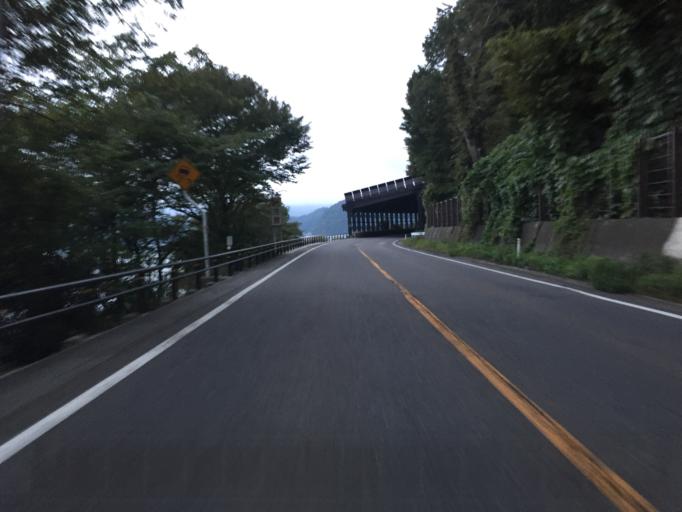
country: JP
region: Fukushima
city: Inawashiro
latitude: 37.5119
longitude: 140.0333
